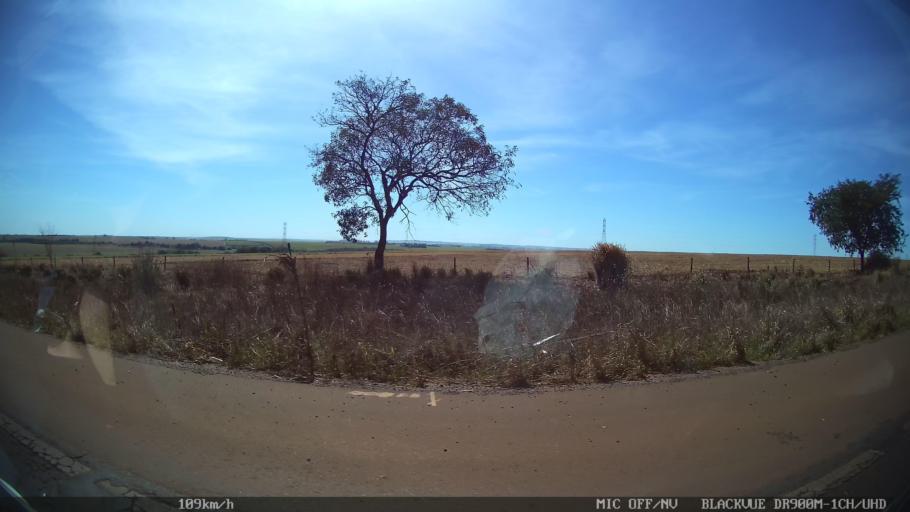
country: BR
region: Sao Paulo
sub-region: Sao Joaquim Da Barra
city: Sao Joaquim da Barra
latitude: -20.5182
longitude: -47.8747
